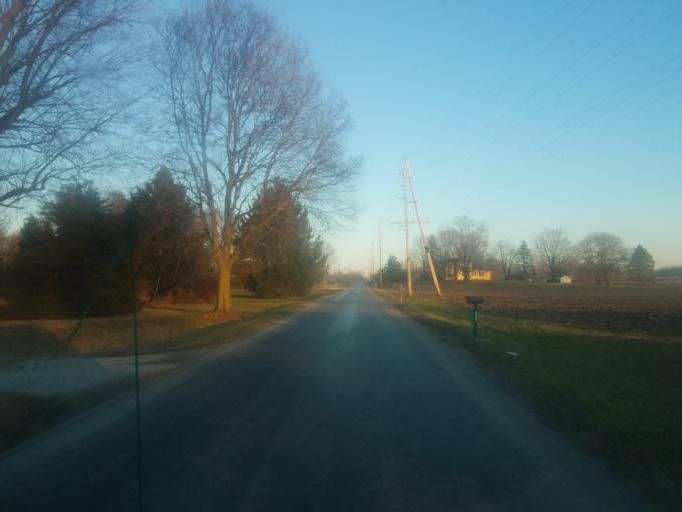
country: US
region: Ohio
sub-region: Wyandot County
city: Upper Sandusky
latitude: 40.8147
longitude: -83.1469
